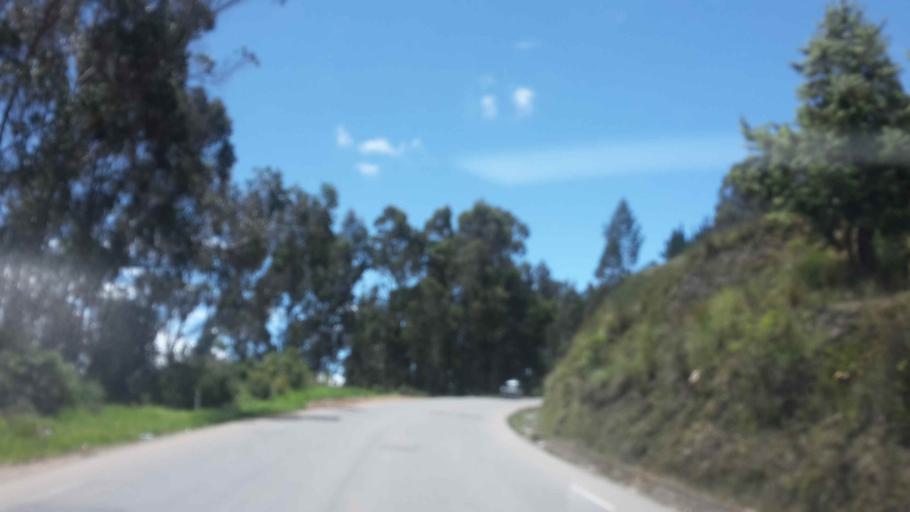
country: BO
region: Cochabamba
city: Colomi
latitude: -17.3200
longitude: -65.8733
